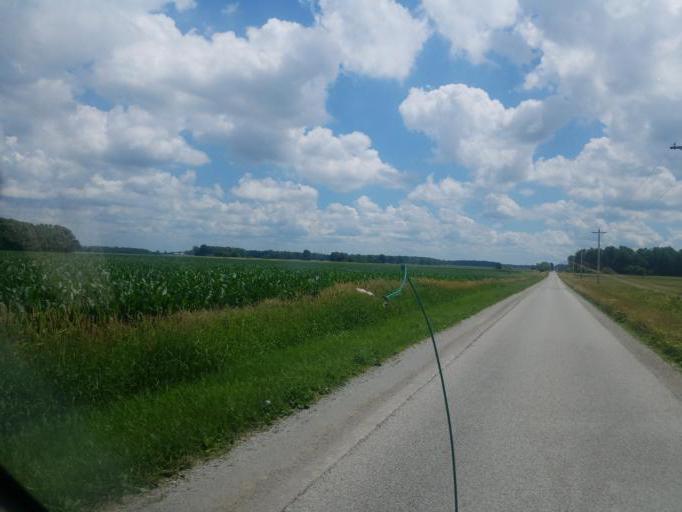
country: US
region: Ohio
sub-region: Huron County
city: Willard
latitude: 41.0385
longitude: -82.8310
